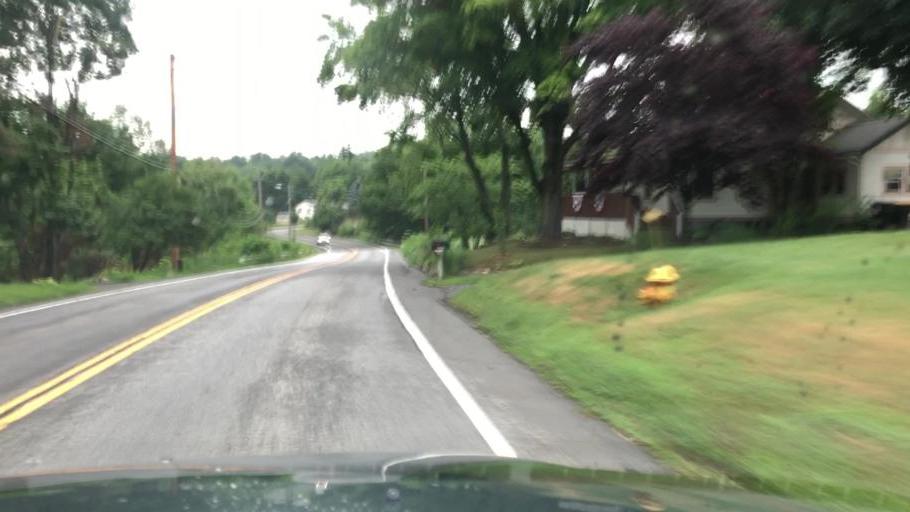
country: US
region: New York
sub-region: Dutchess County
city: Beacon
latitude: 41.5224
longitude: -73.9407
